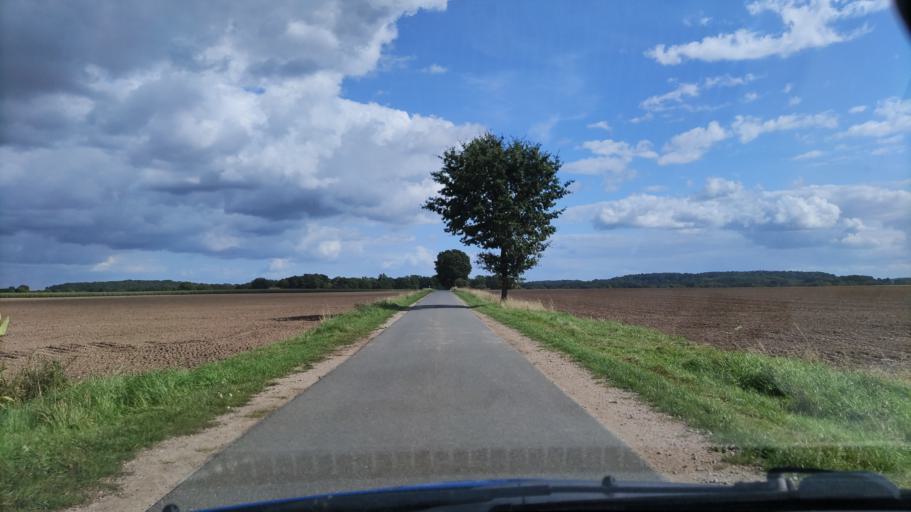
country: DE
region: Lower Saxony
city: Romstedt
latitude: 53.0785
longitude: 10.6585
